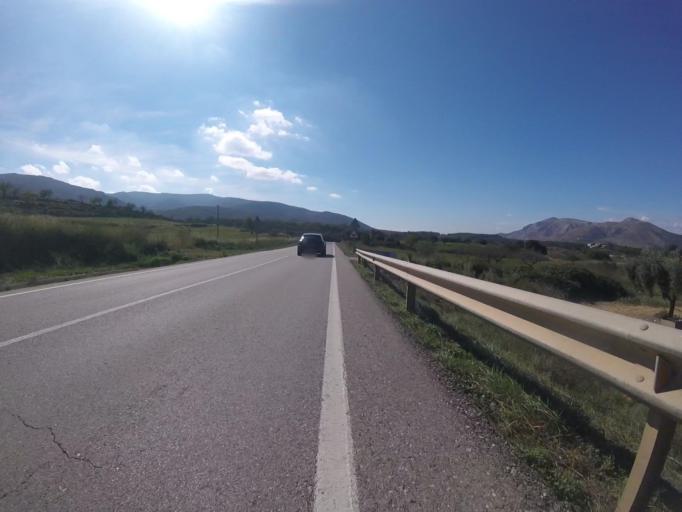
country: ES
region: Valencia
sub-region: Provincia de Castello
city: Albocasser
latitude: 40.3345
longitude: -0.0131
